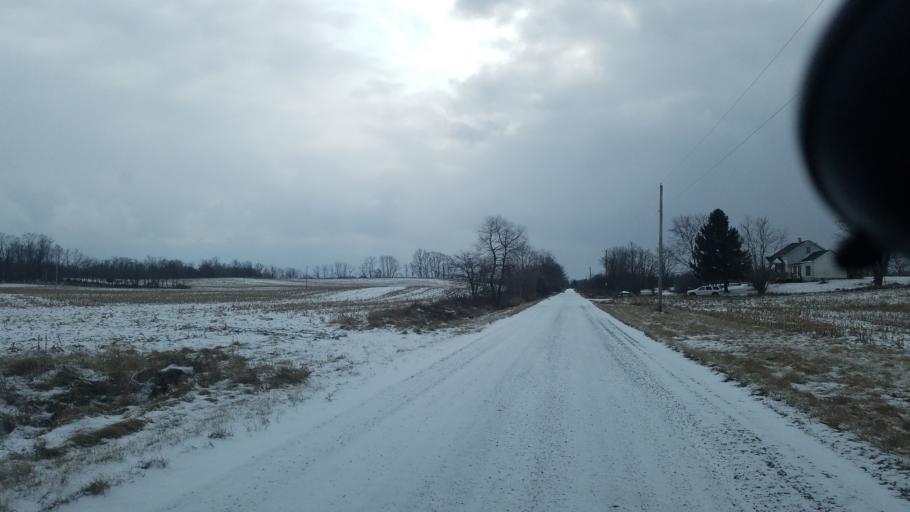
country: US
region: Ohio
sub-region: Morrow County
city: Mount Gilead
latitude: 40.5473
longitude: -82.7106
